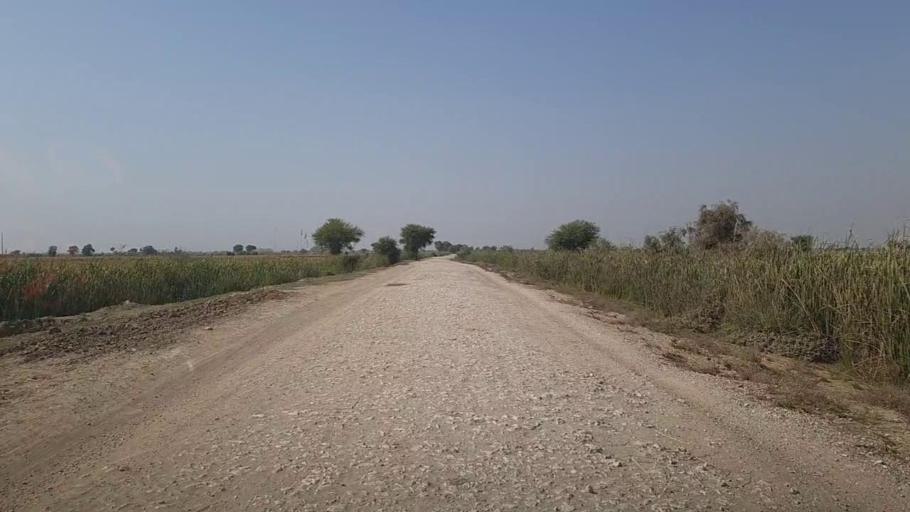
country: PK
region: Sindh
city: Kandhkot
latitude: 28.3995
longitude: 69.2660
